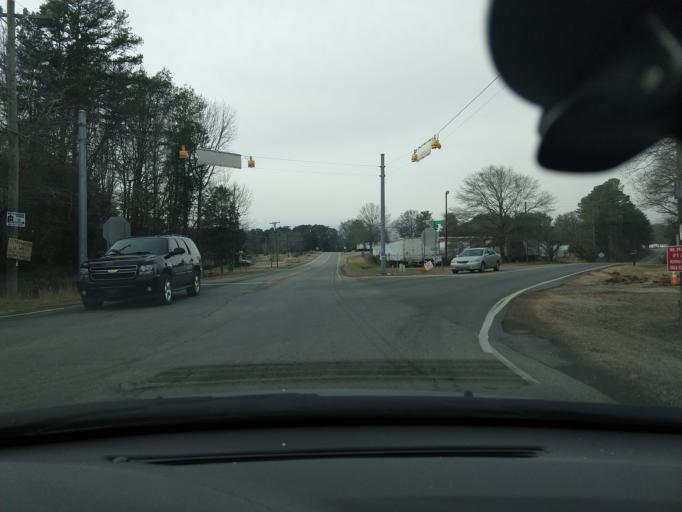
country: US
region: South Carolina
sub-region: Spartanburg County
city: Cowpens
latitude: 35.0090
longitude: -81.8528
